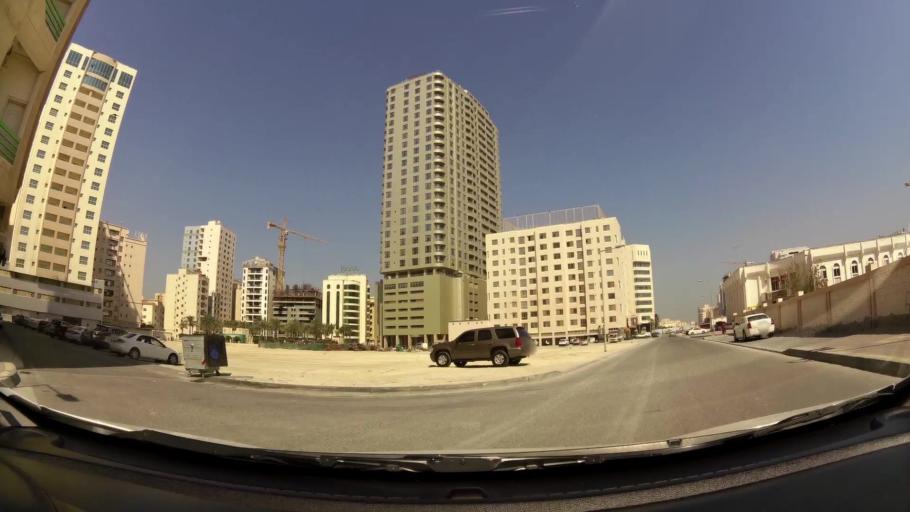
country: BH
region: Manama
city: Manama
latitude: 26.2130
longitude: 50.6002
